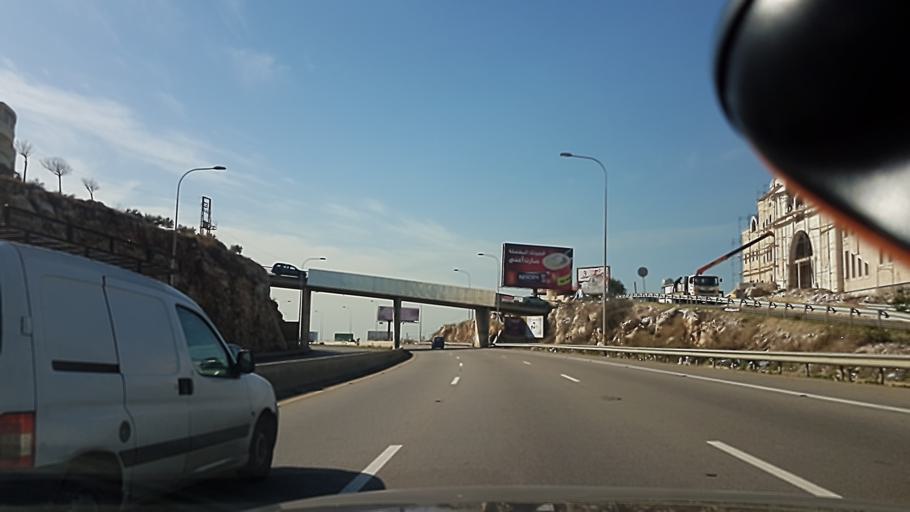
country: LB
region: Liban-Sud
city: Sidon
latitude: 33.6052
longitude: 35.3931
